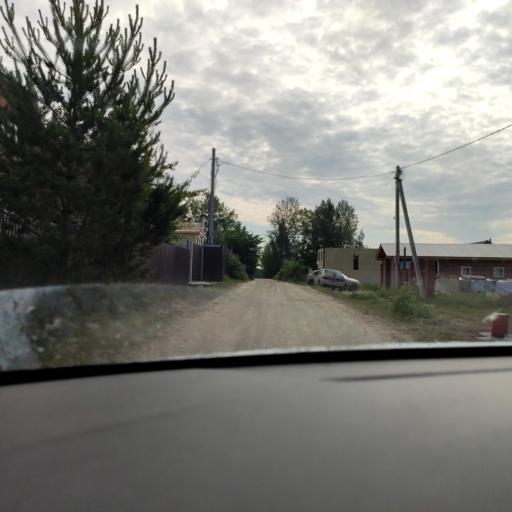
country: RU
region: Tatarstan
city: Pestretsy
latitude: 55.7131
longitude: 49.4581
